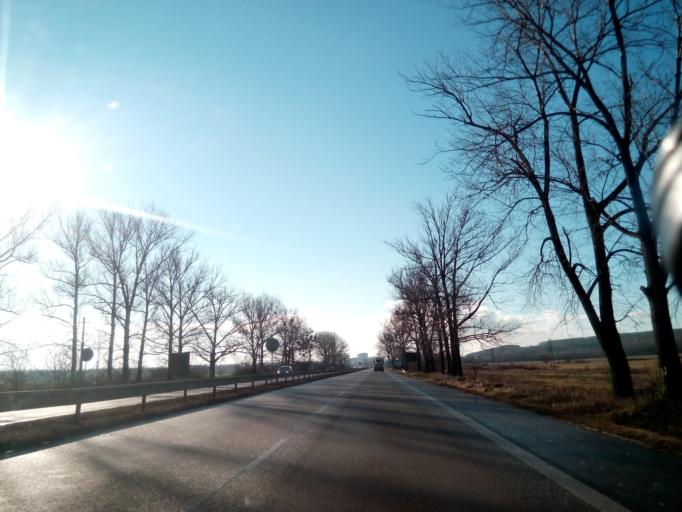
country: SK
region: Kosicky
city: Kosice
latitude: 48.6581
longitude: 21.2064
